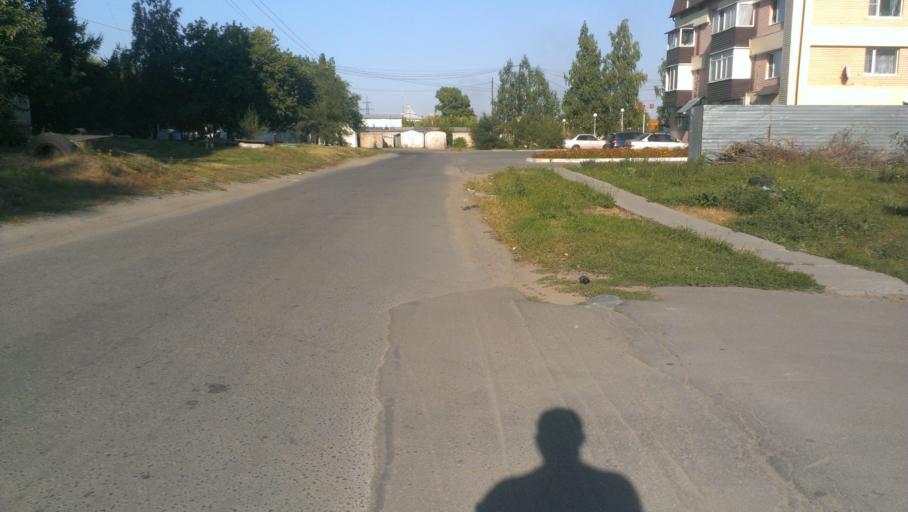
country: RU
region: Altai Krai
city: Novosilikatnyy
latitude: 53.3050
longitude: 83.6253
